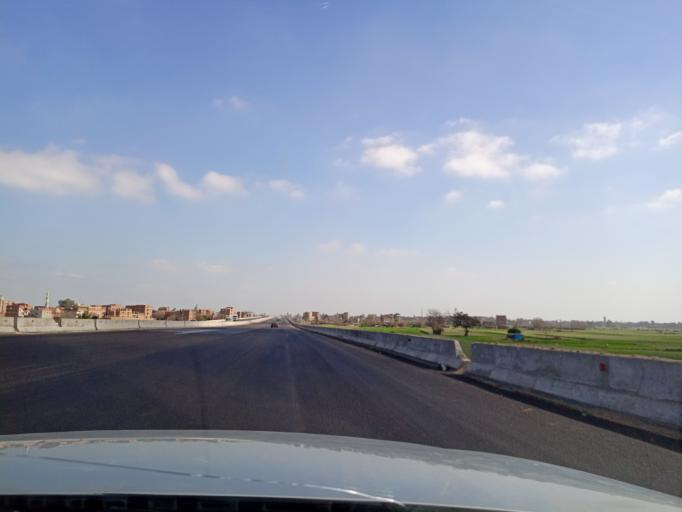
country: EG
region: Muhafazat al Minufiyah
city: Al Bajur
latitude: 30.4135
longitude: 31.0636
